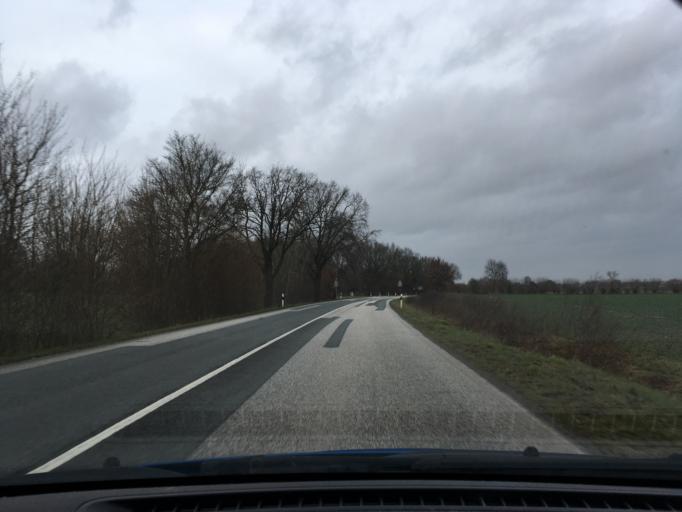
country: DE
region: Schleswig-Holstein
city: Kruzen
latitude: 53.4132
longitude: 10.5363
